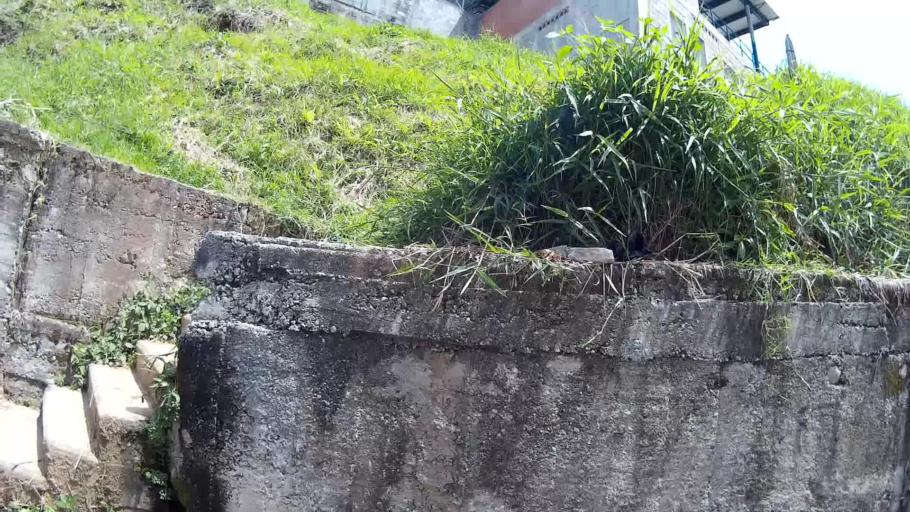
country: CO
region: Antioquia
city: Medellin
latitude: 6.2704
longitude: -75.6294
